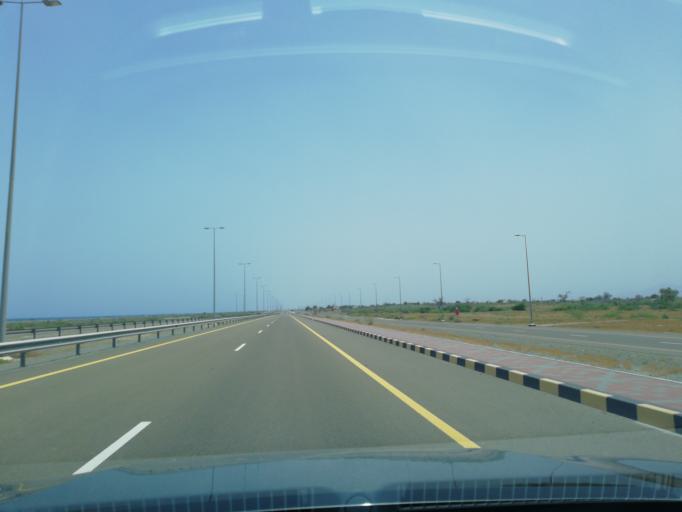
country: OM
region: Al Batinah
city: Shinas
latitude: 24.9050
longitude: 56.3943
